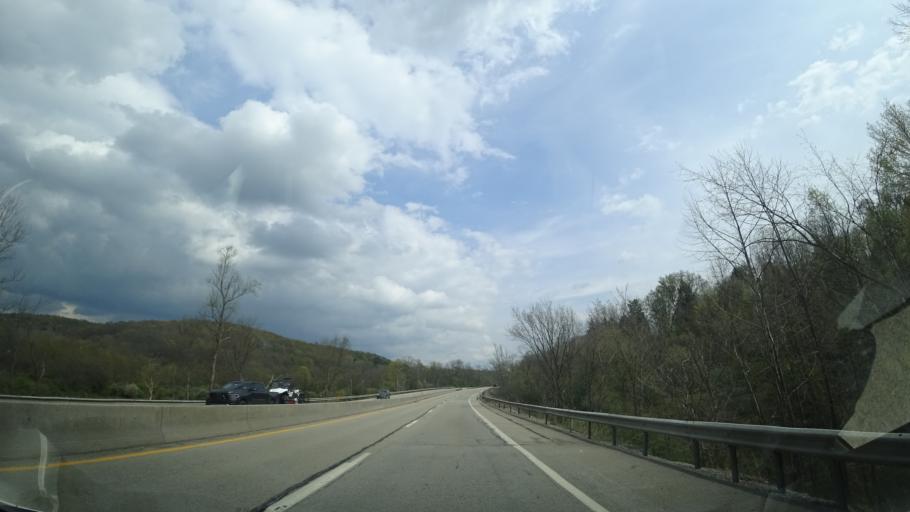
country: US
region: Pennsylvania
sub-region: Fayette County
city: Oliver
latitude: 39.9741
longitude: -79.7578
